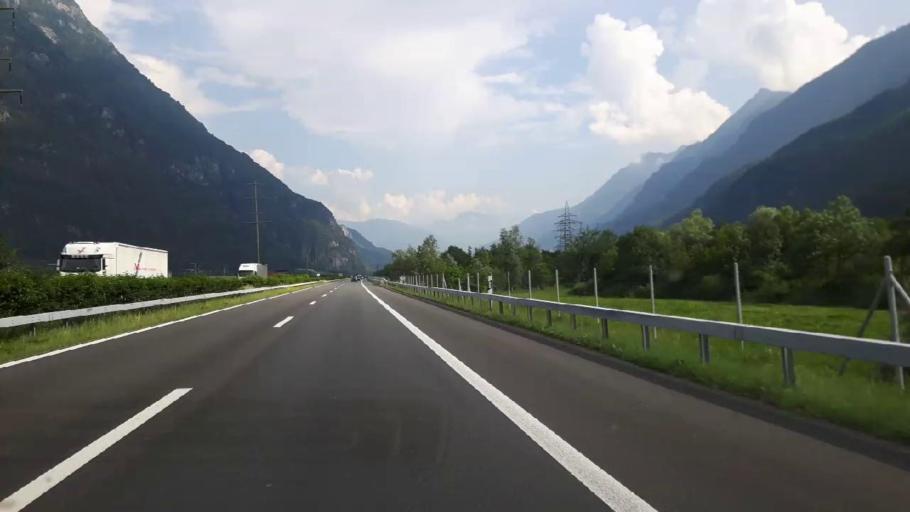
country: CH
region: Ticino
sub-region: Riviera District
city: Biasca
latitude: 46.3455
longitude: 8.9664
